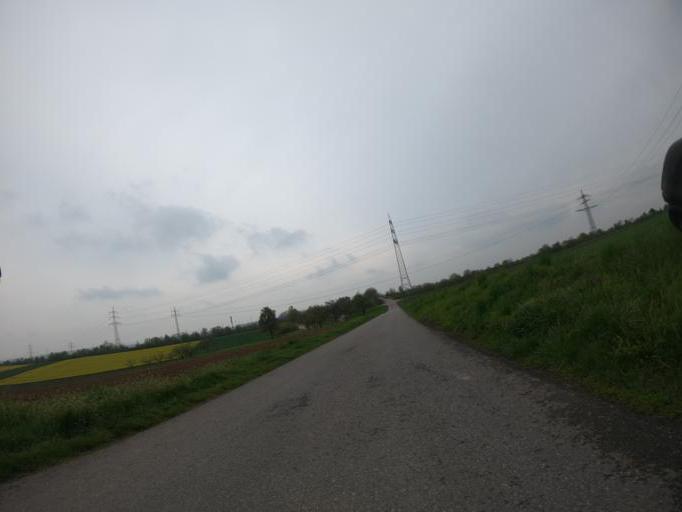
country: DE
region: Baden-Wuerttemberg
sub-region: Regierungsbezirk Stuttgart
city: Schwieberdingen
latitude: 48.8891
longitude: 9.0767
